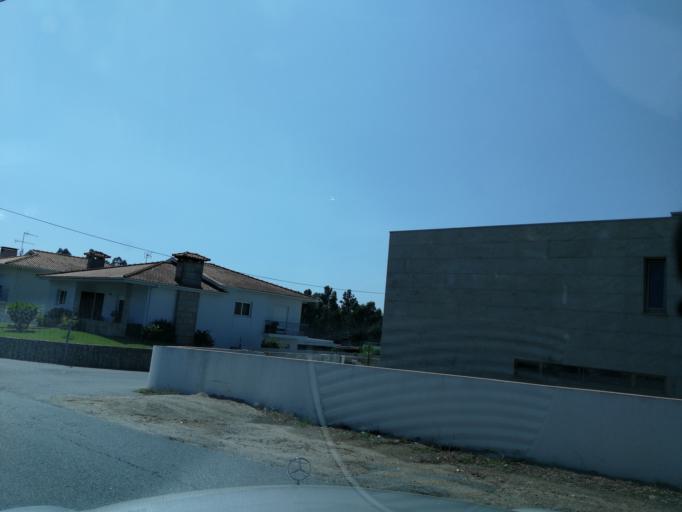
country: PT
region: Braga
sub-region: Braga
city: Adaufe
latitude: 41.5541
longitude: -8.3482
